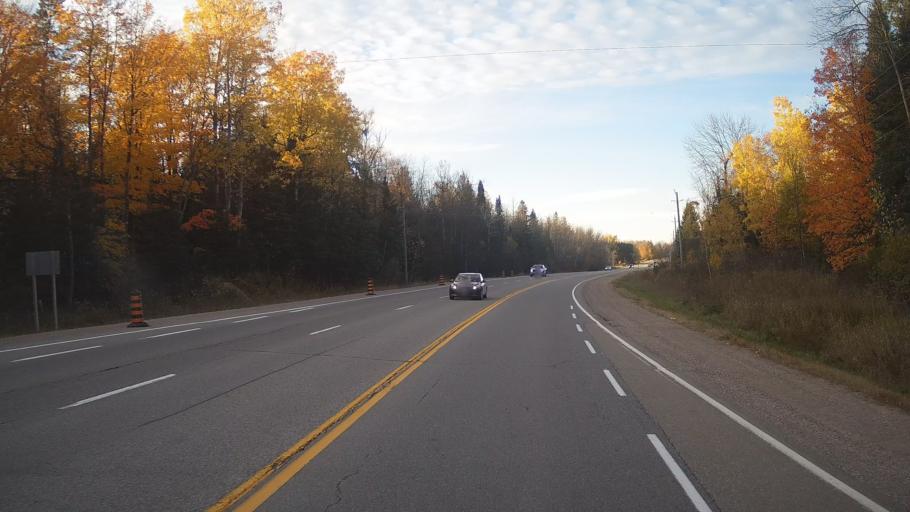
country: CA
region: Ontario
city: Perth
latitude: 45.0306
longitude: -76.2447
